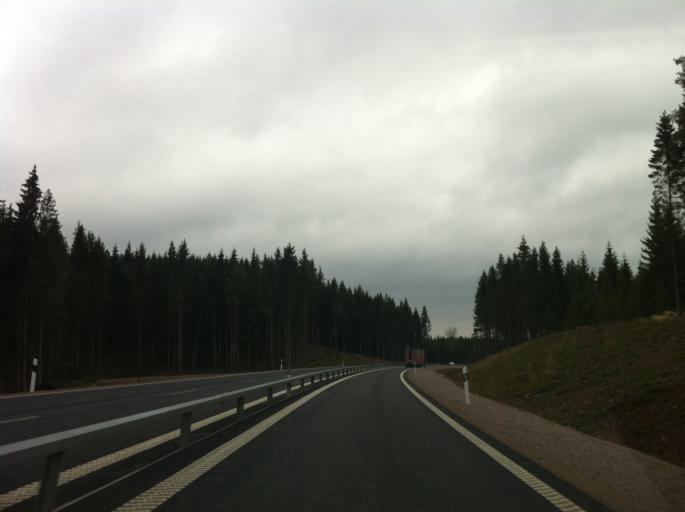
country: SE
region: Joenkoeping
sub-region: Vetlanda Kommun
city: Vetlanda
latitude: 57.4246
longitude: 15.1864
